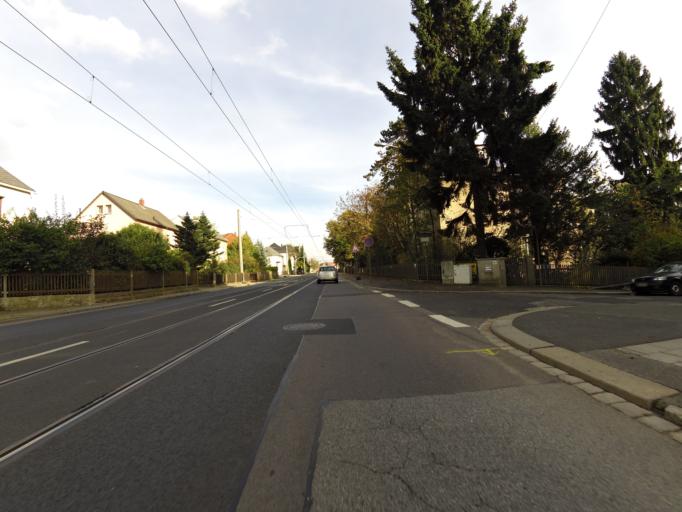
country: DE
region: Saxony
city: Albertstadt
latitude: 51.0621
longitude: 13.8416
